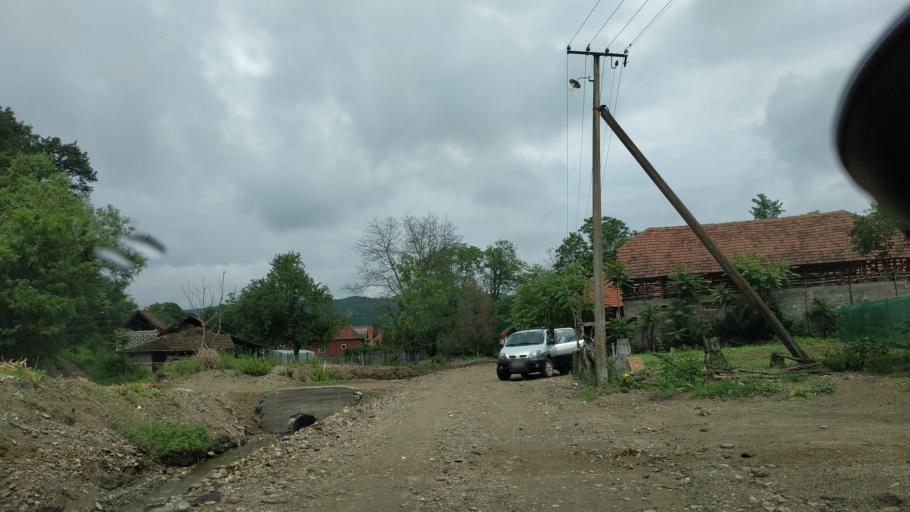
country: RS
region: Central Serbia
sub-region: Nisavski Okrug
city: Aleksinac
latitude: 43.4266
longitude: 21.6530
